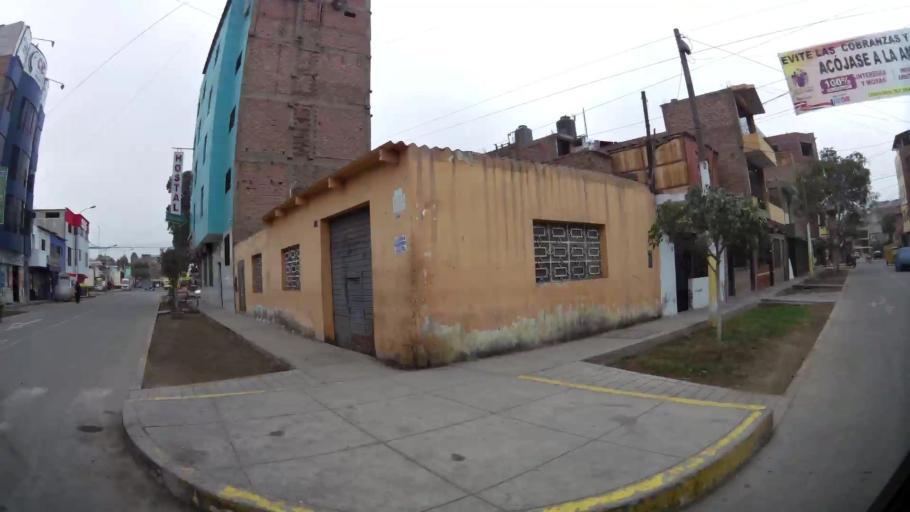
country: PE
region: Lima
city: Ventanilla
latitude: -11.8673
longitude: -77.0787
